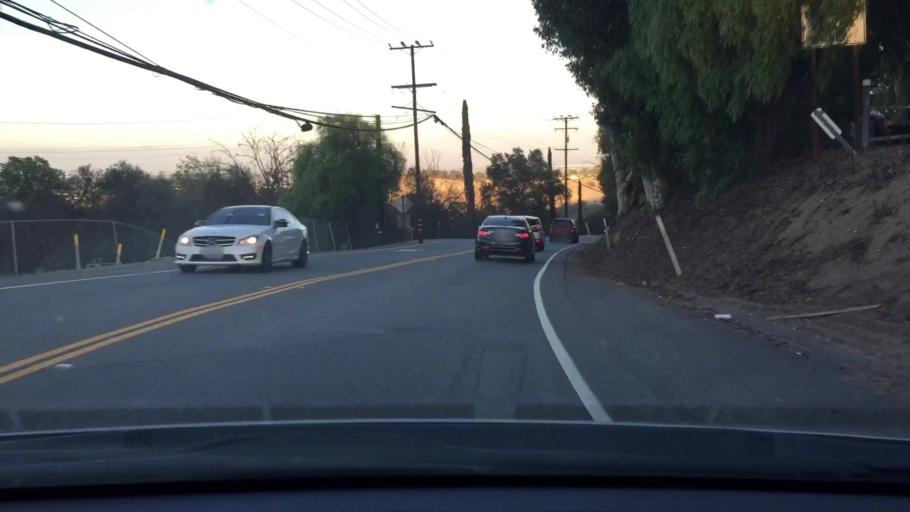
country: US
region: California
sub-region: San Bernardino County
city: Chino Hills
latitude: 33.9670
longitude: -117.7593
